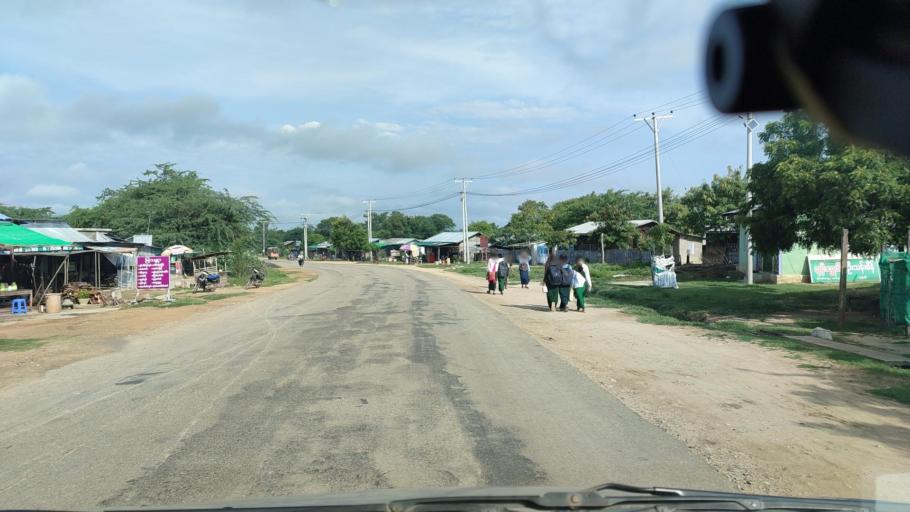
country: MM
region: Mandalay
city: Meiktila
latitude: 20.9652
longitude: 95.7527
